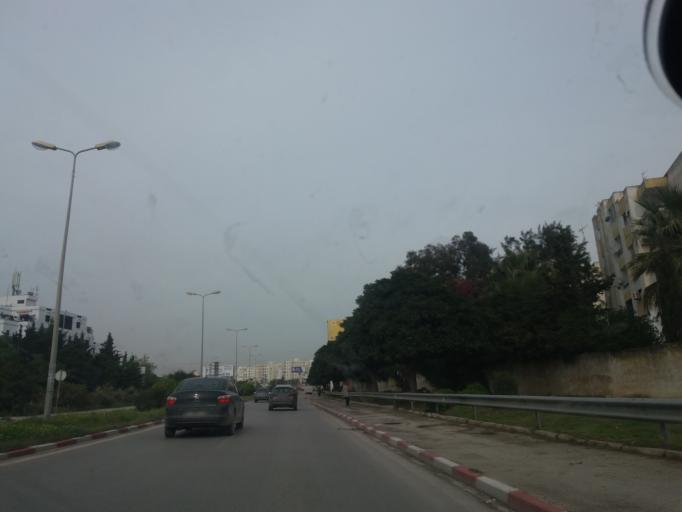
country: TN
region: Tunis
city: Tunis
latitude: 36.8493
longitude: 10.1568
